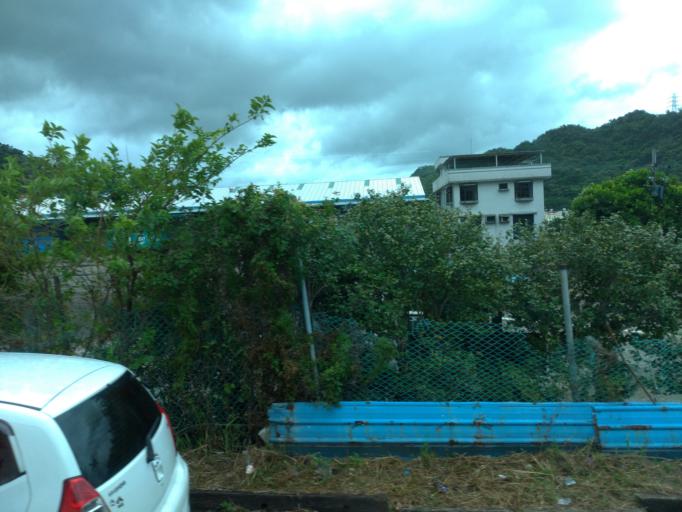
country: TW
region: Taiwan
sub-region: Keelung
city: Keelung
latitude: 25.0967
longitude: 121.7488
